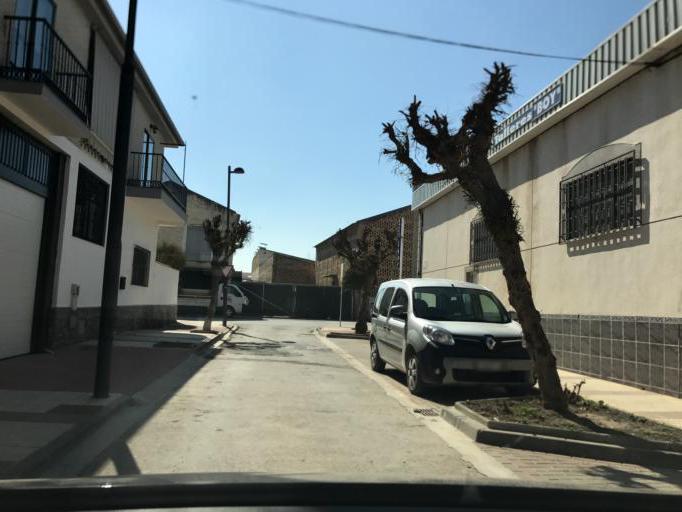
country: ES
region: Andalusia
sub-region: Provincia de Granada
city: Chauchina
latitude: 37.1937
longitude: -3.7739
